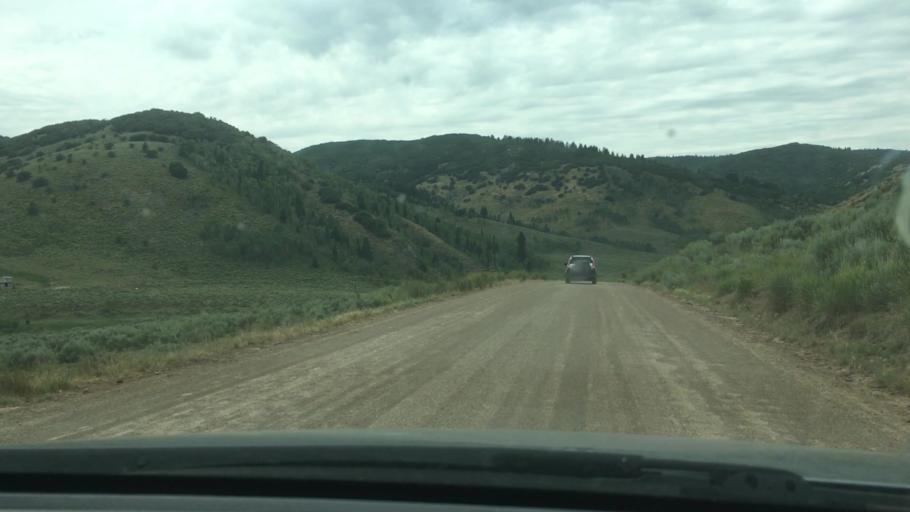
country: US
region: Utah
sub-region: Summit County
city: Summit Park
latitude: 40.7813
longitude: -111.5902
